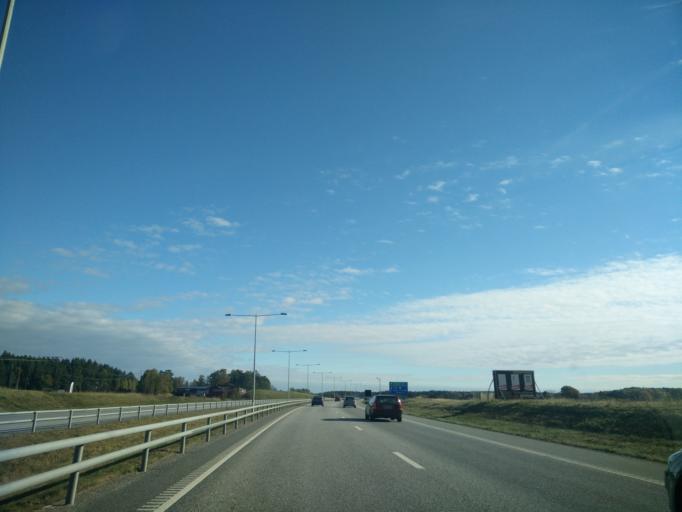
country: SE
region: Stockholm
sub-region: Taby Kommun
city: Taby
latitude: 59.4755
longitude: 18.0234
